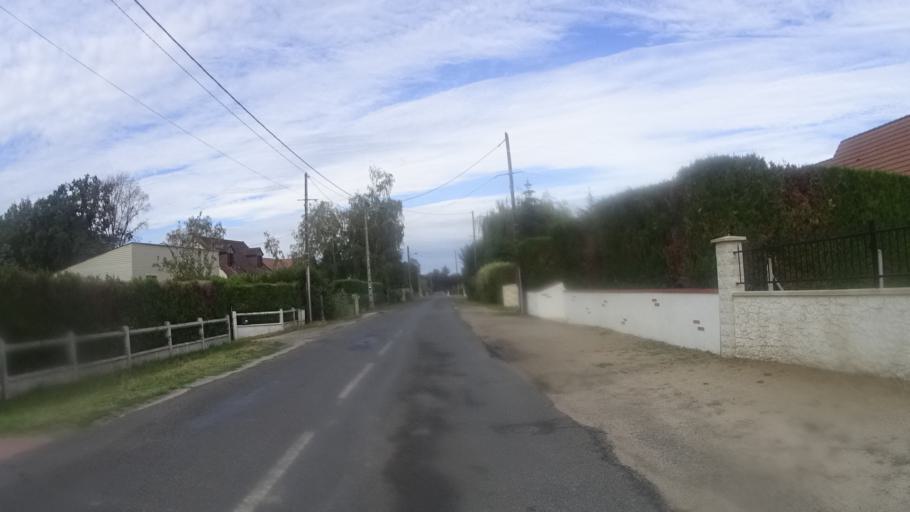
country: FR
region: Centre
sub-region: Departement du Loiret
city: Fay-aux-Loges
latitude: 47.9385
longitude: 2.1780
